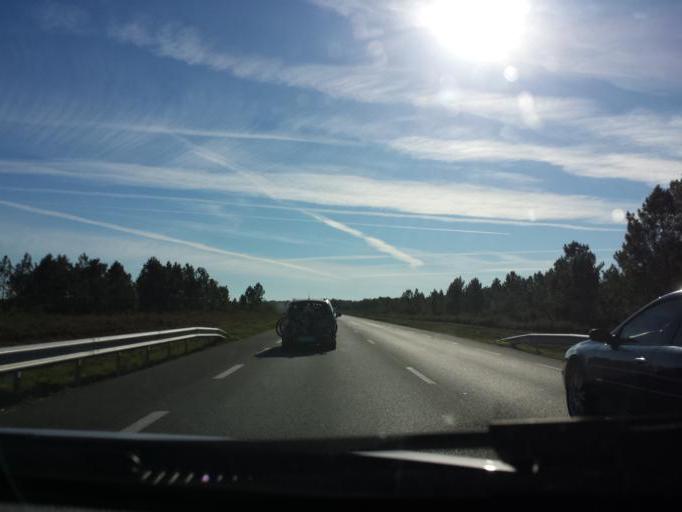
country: FR
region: Aquitaine
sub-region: Departement de la Gironde
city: Lacanau
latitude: 44.9943
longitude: -1.0853
